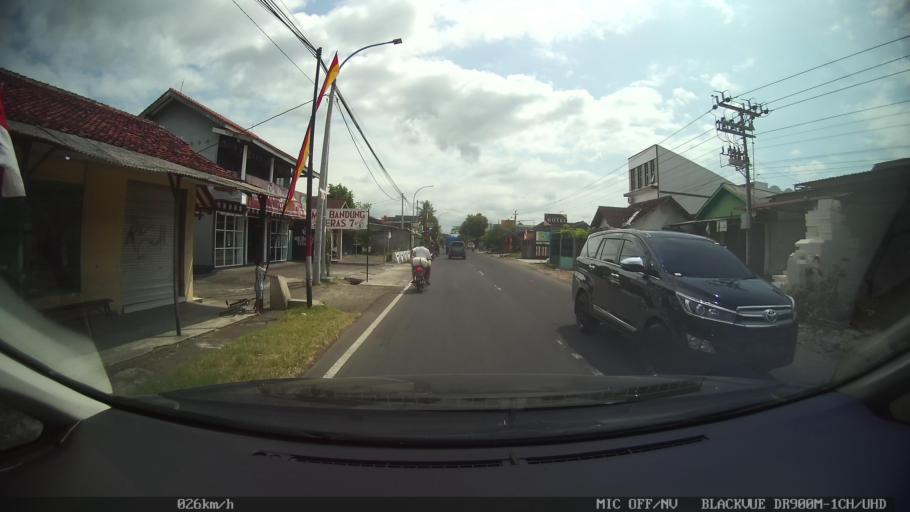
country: ID
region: Daerah Istimewa Yogyakarta
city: Depok
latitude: -7.8353
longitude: 110.4769
